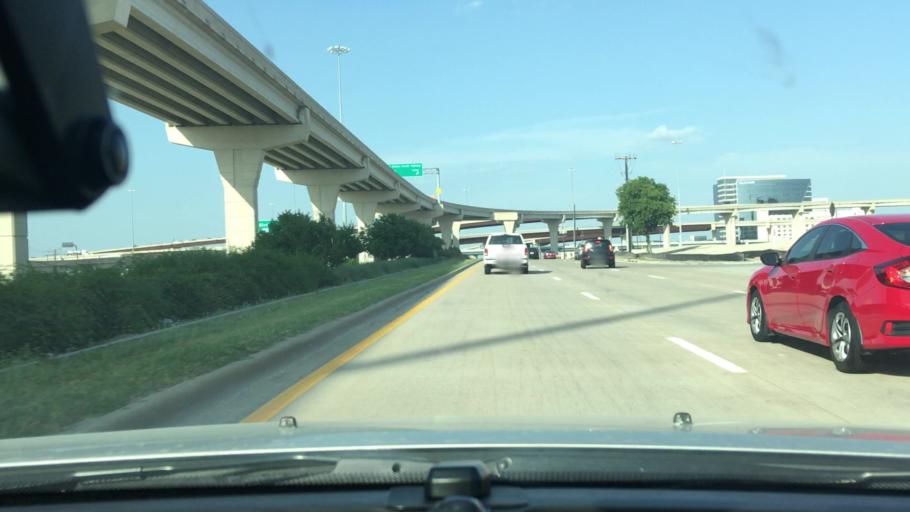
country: US
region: Texas
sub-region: Denton County
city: The Colony
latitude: 33.0890
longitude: -96.8282
